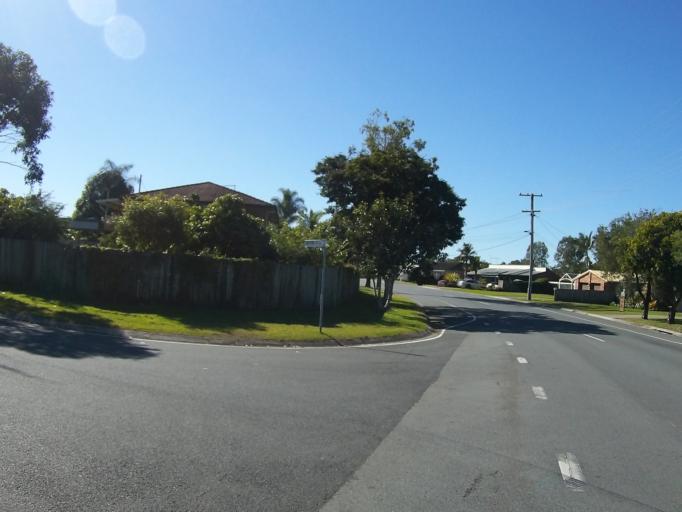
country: AU
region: Queensland
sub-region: Logan
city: Windaroo
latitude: -27.7316
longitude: 153.2124
